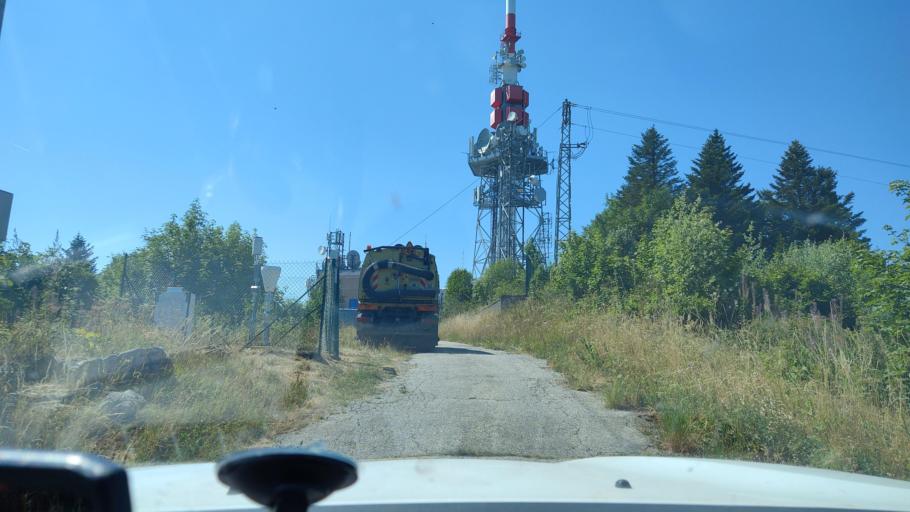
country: FR
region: Rhone-Alpes
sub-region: Departement de la Savoie
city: Le Bourget-du-Lac
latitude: 45.6607
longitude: 5.8216
